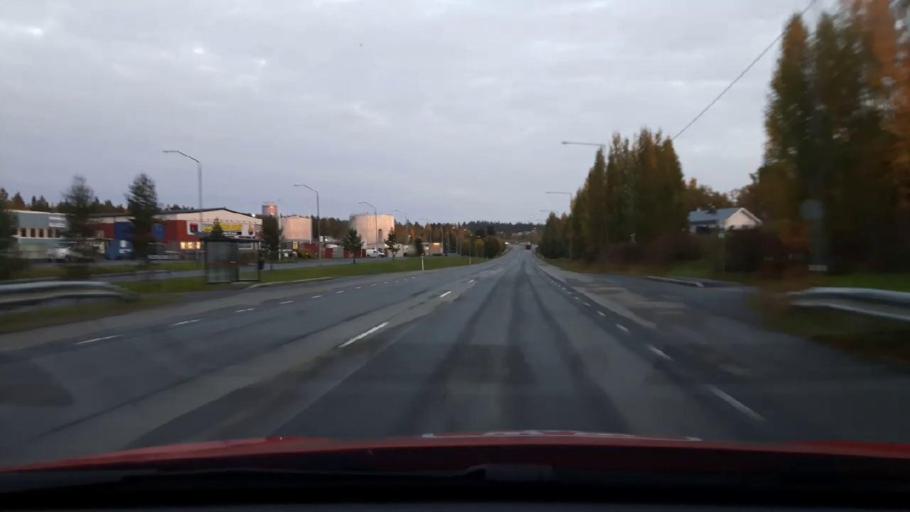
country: SE
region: Jaemtland
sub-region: OEstersunds Kommun
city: Ostersund
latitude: 63.2045
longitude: 14.6406
